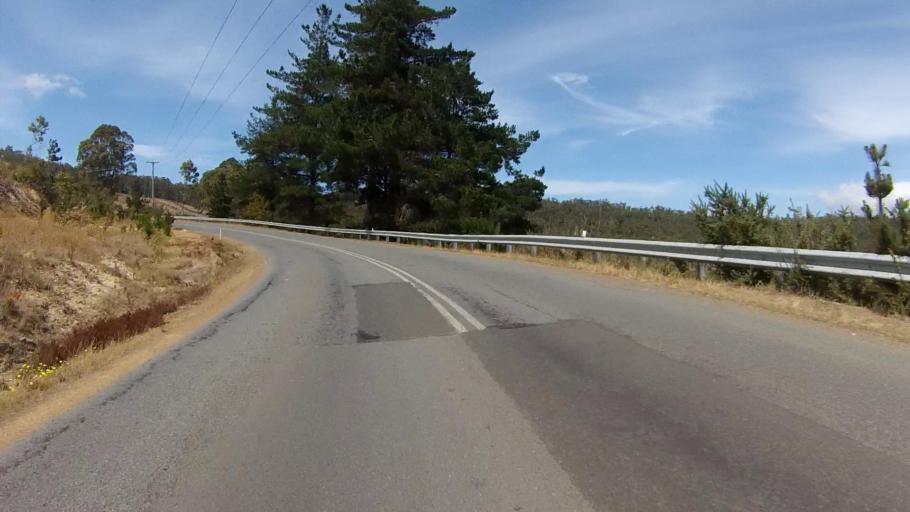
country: AU
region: Tasmania
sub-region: Huon Valley
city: Cygnet
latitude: -43.2189
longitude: 147.1219
